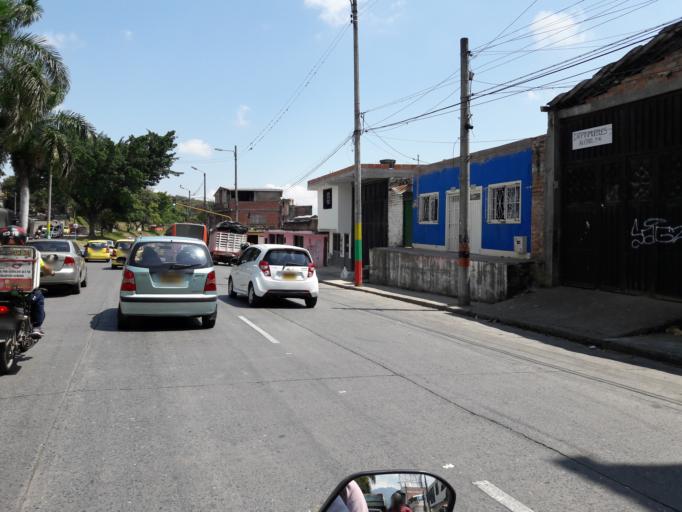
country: CO
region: Tolima
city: Ibague
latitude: 4.4366
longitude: -75.2237
